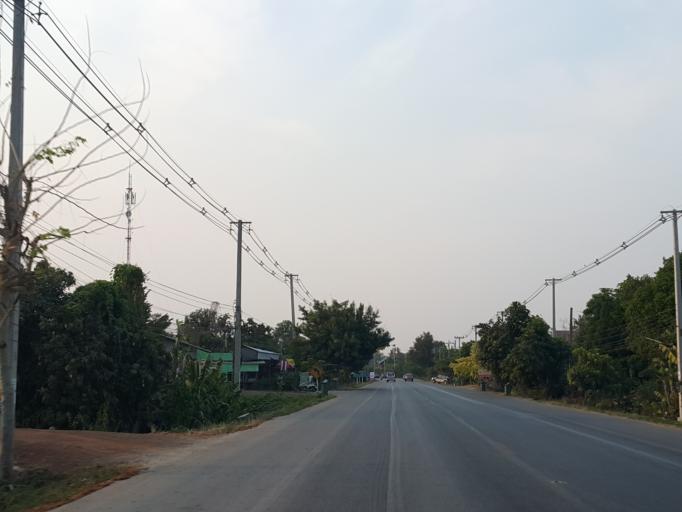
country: TH
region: Sukhothai
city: Sawankhalok
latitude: 17.2469
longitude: 99.8583
